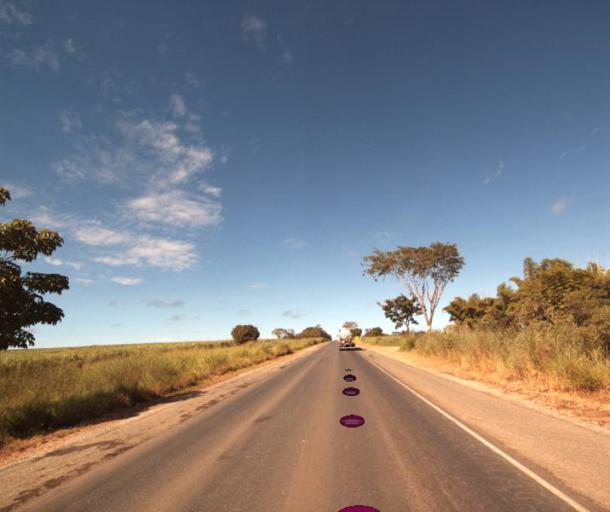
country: BR
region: Goias
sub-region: Itapaci
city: Itapaci
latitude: -14.8300
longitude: -49.3037
